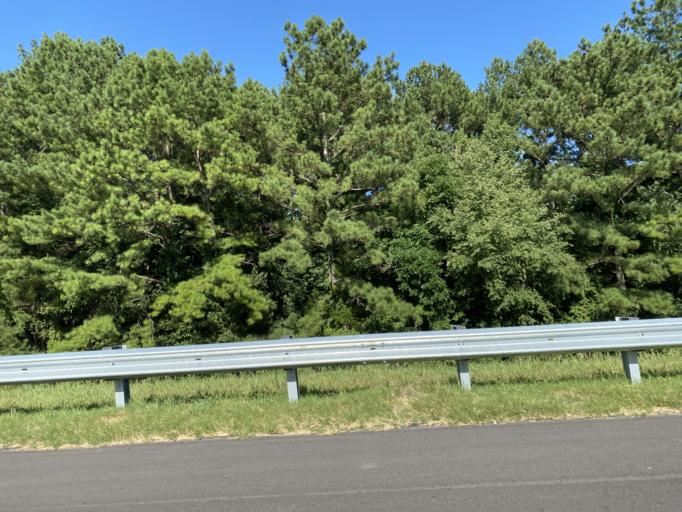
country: US
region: Alabama
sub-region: Limestone County
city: Athens
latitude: 34.7570
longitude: -86.9381
